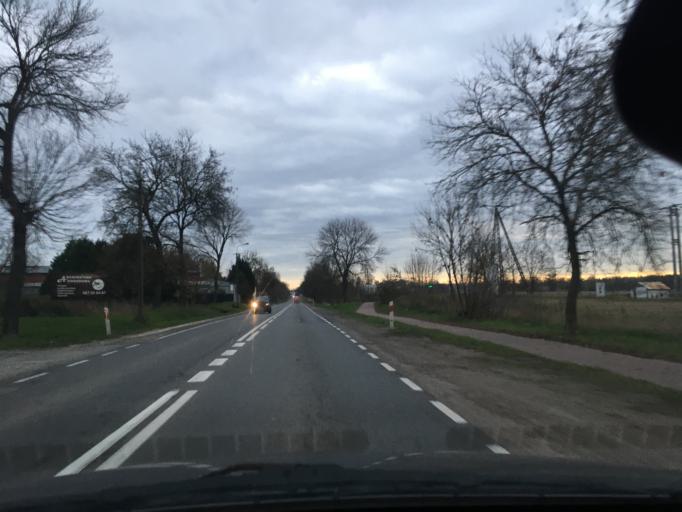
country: PL
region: Masovian Voivodeship
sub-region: Powiat piaseczynski
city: Lesznowola
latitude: 52.0951
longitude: 20.9253
